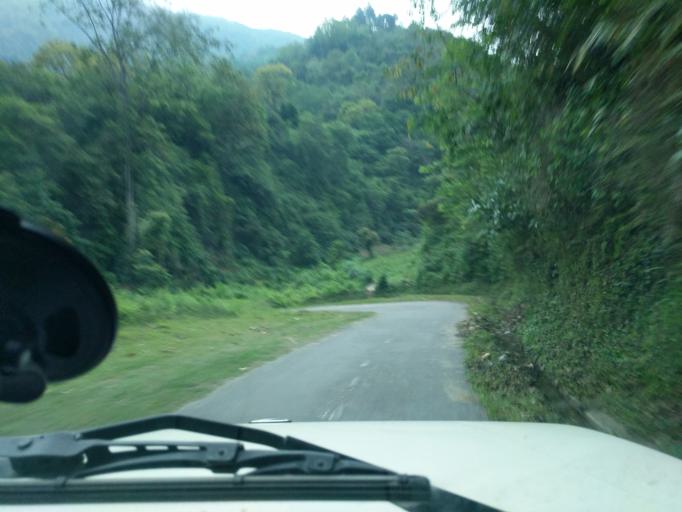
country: BT
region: Mongar
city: Mongar
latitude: 27.2931
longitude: 91.1452
